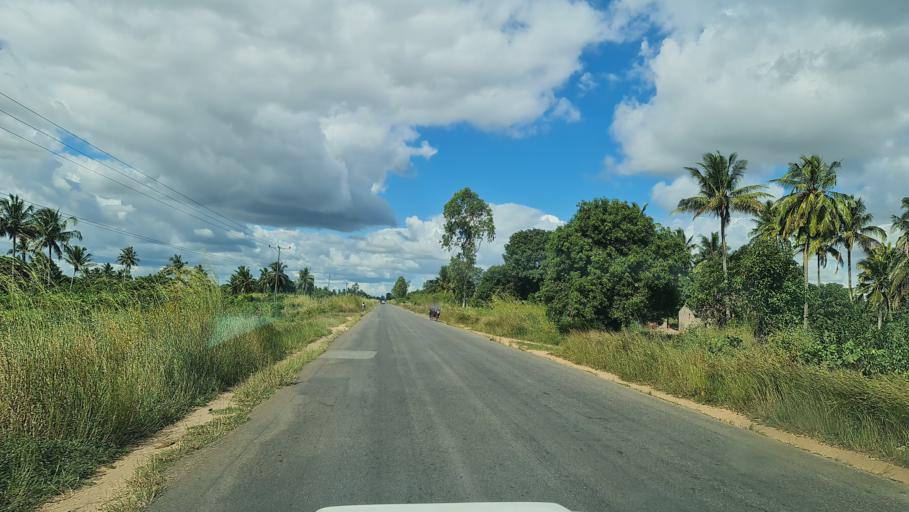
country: MZ
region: Zambezia
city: Quelimane
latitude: -17.5894
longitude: 36.7603
